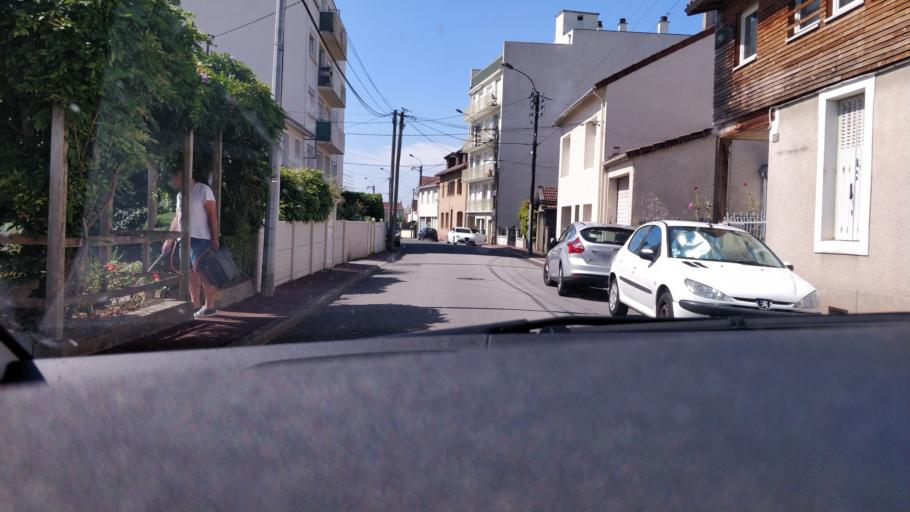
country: FR
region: Limousin
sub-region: Departement de la Haute-Vienne
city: Limoges
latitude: 45.8505
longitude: 1.2515
